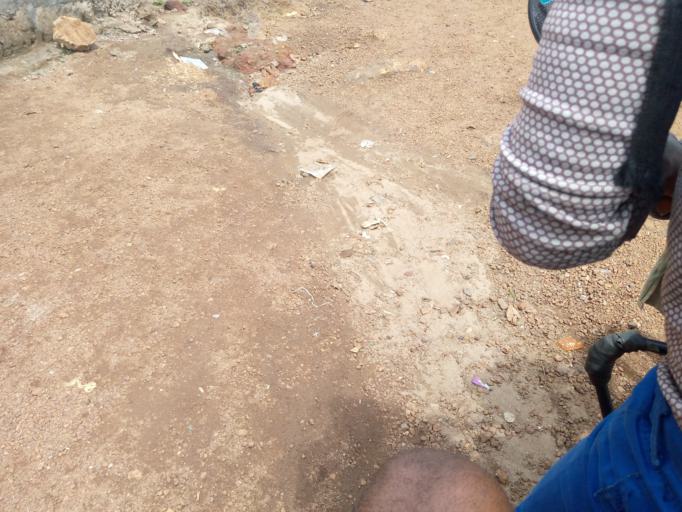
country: SL
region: Western Area
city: Hastings
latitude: 8.4144
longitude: -13.1413
